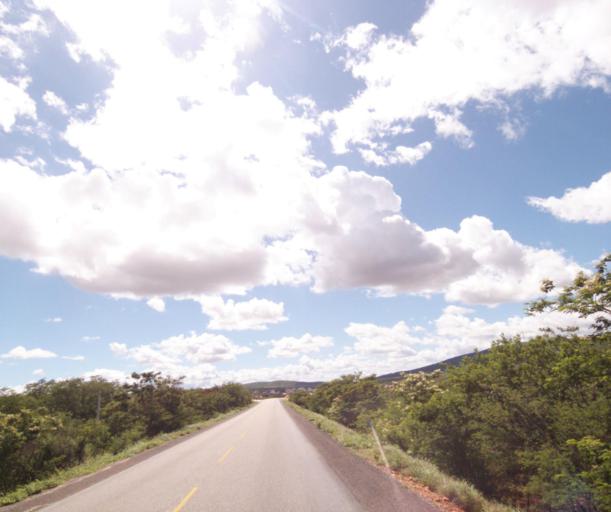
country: BR
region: Bahia
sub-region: Cacule
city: Cacule
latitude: -14.2092
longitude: -42.1022
